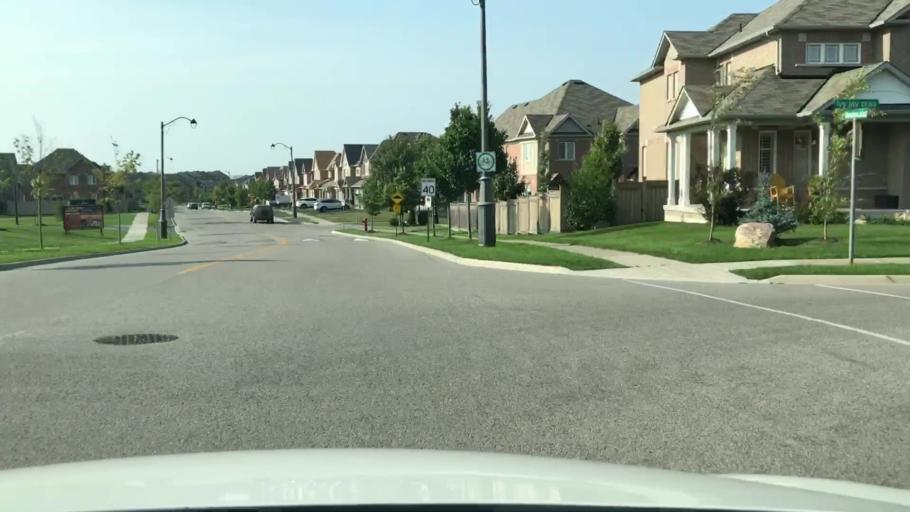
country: CA
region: Ontario
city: Newmarket
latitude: 44.0146
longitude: -79.4369
